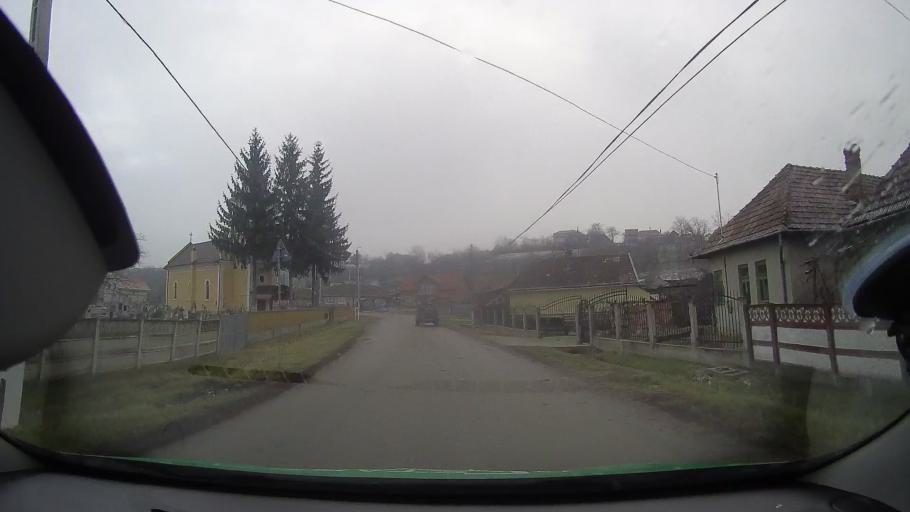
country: RO
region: Alba
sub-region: Comuna Noslac
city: Noslac
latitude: 46.4101
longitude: 23.9414
